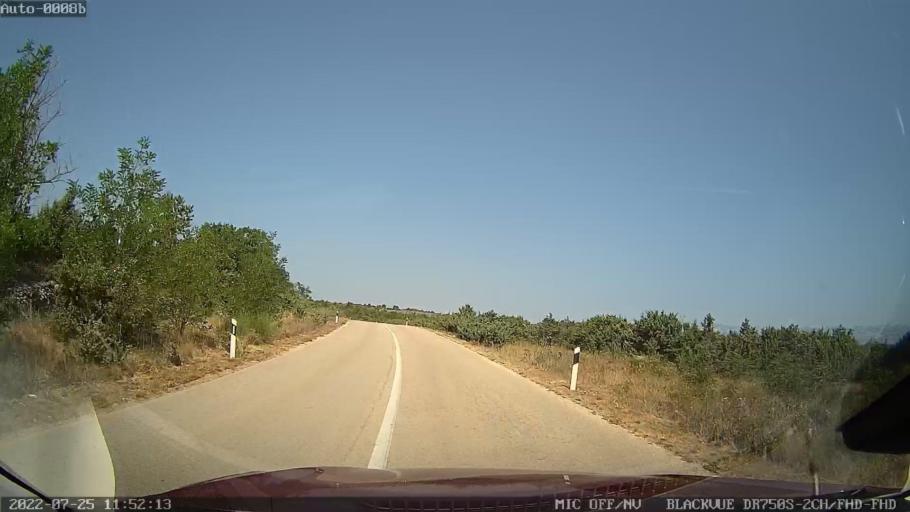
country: HR
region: Zadarska
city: Vrsi
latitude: 44.2462
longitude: 15.2464
